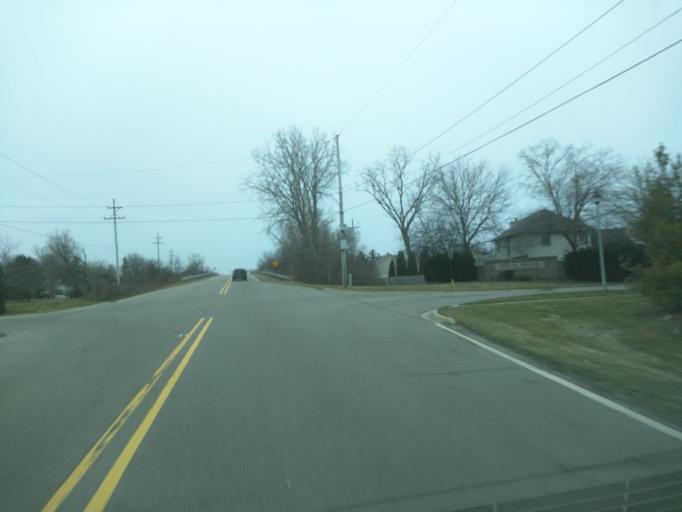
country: US
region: Michigan
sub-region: Eaton County
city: Waverly
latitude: 42.7227
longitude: -84.6228
